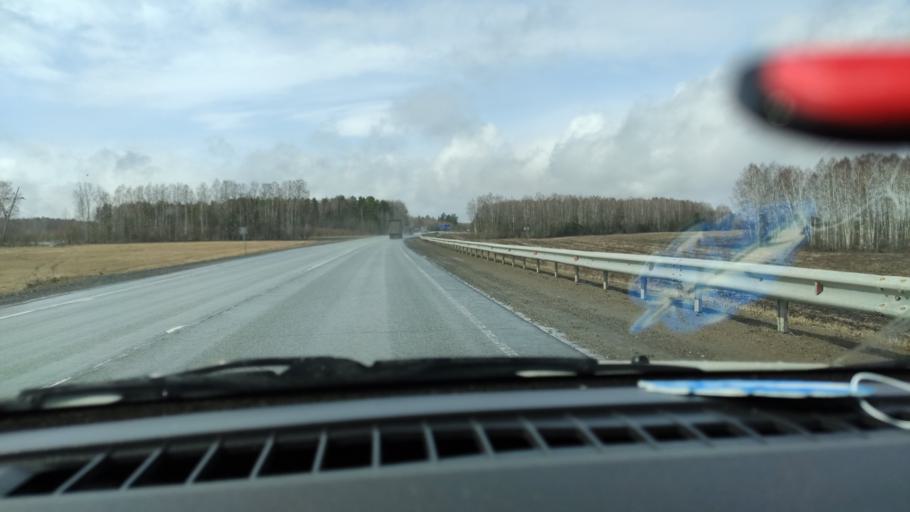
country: RU
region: Sverdlovsk
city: Ufimskiy
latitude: 56.7752
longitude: 57.9978
